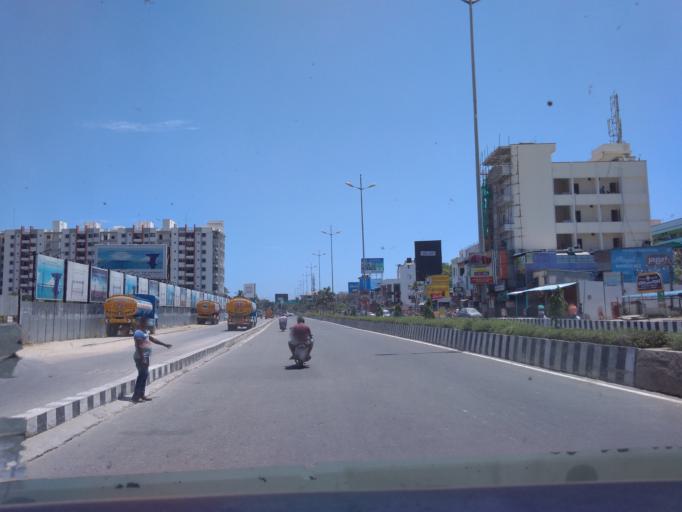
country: IN
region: Tamil Nadu
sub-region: Kancheepuram
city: Injambakkam
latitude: 12.8350
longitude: 80.2287
